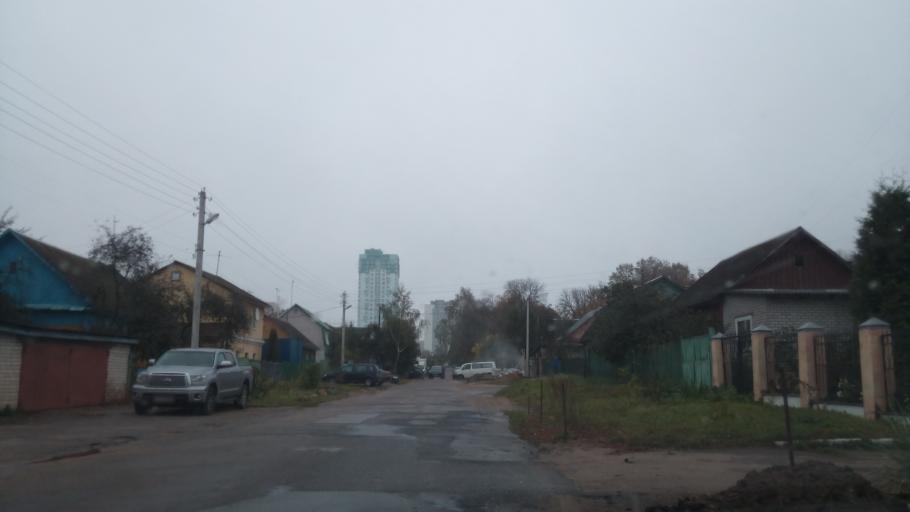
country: BY
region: Minsk
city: Minsk
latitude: 53.9425
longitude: 27.5882
